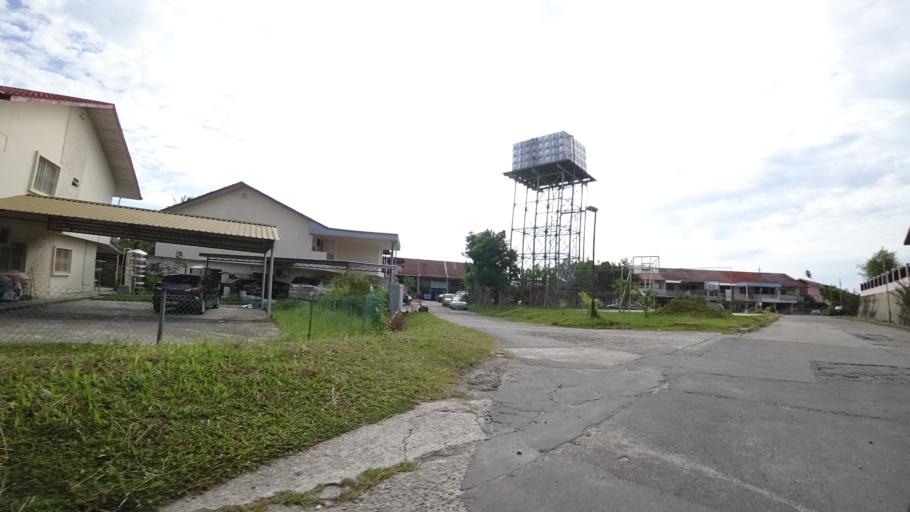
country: BN
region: Brunei and Muara
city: Bandar Seri Begawan
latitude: 4.8870
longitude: 114.9238
